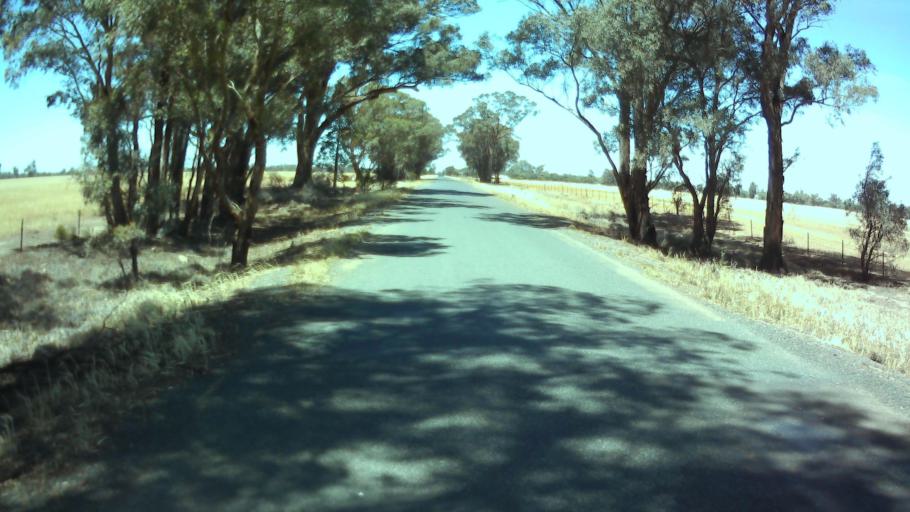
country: AU
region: New South Wales
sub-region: Weddin
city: Grenfell
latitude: -34.0233
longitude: 147.7922
